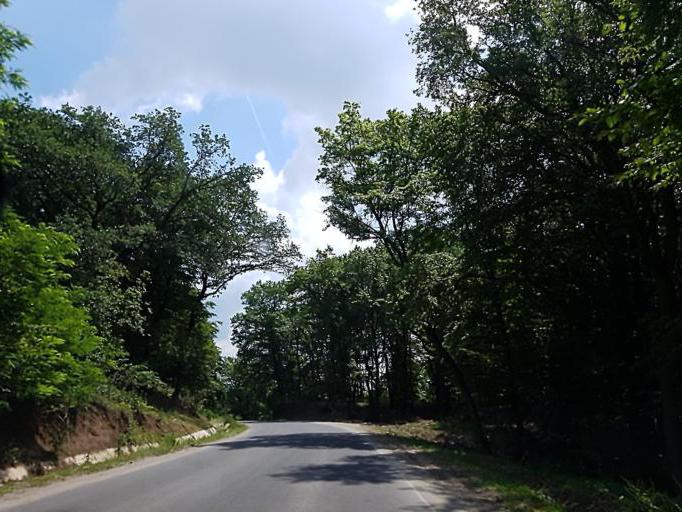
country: RO
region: Sibiu
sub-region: Comuna Seica Mare
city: Seica Mare
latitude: 46.0408
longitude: 24.1577
